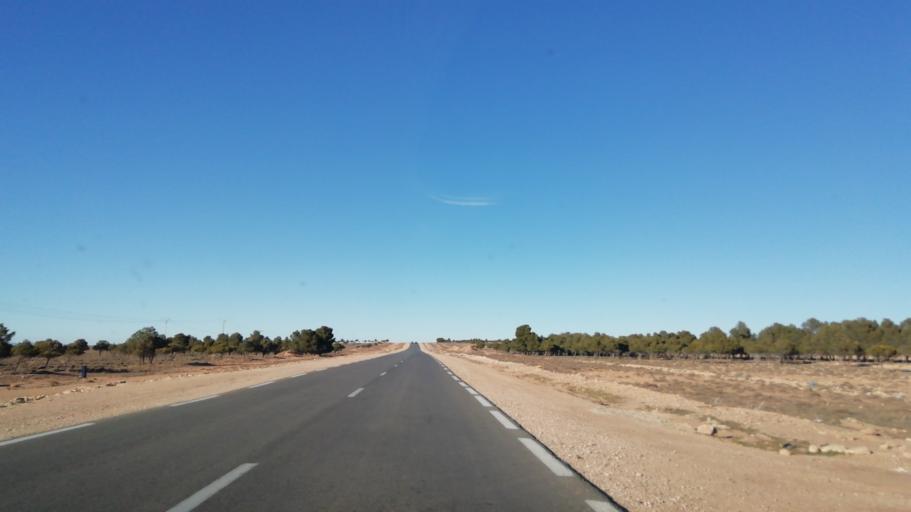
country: DZ
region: Tlemcen
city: Sebdou
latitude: 34.2526
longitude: -1.2574
